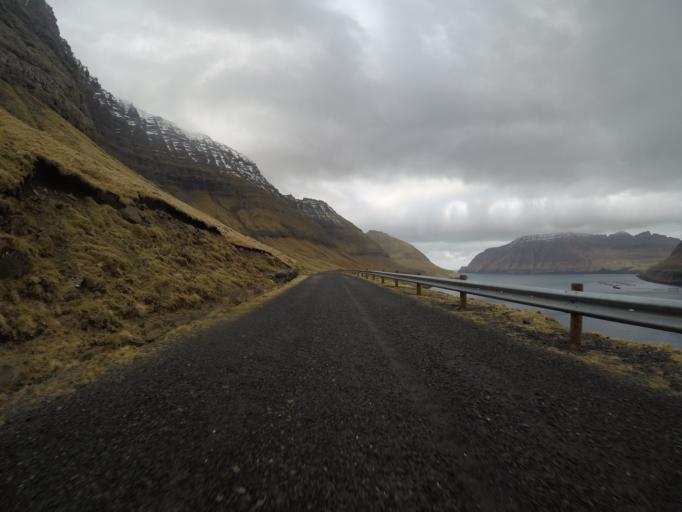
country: FO
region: Nordoyar
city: Klaksvik
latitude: 62.3290
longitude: -6.5701
